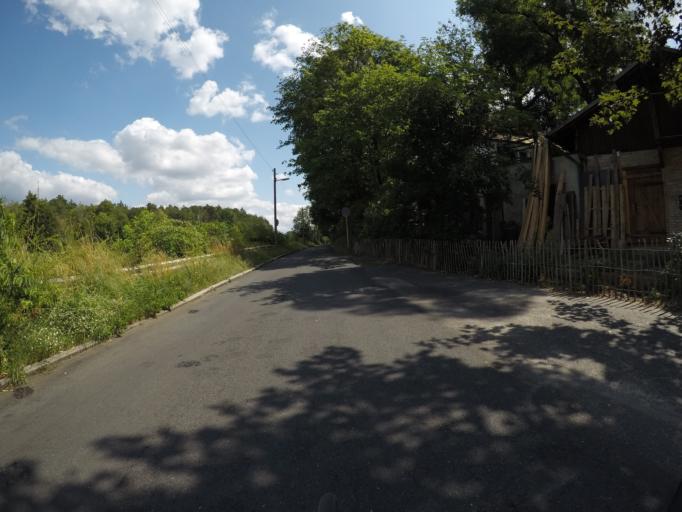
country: DE
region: Berlin
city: Wannsee
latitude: 52.3965
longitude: 13.1507
